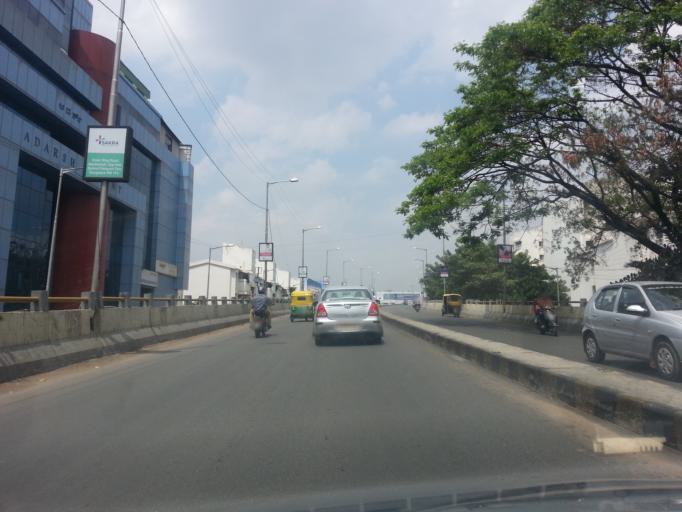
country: IN
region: Karnataka
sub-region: Bangalore Urban
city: Bangalore
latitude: 12.9589
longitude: 77.6414
